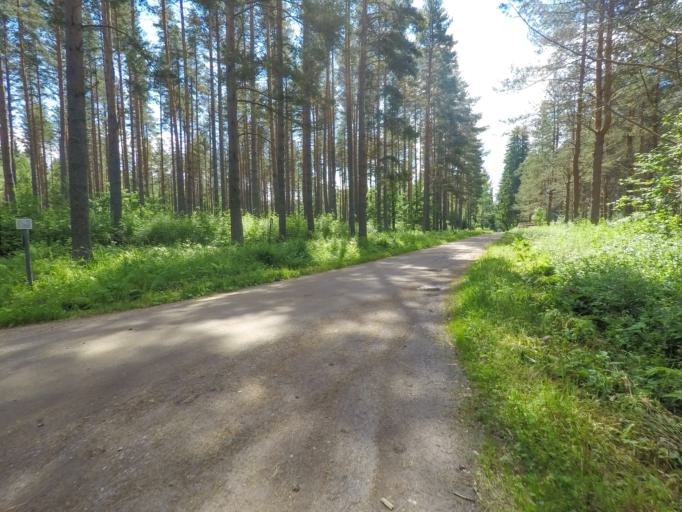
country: FI
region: Southern Savonia
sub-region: Savonlinna
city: Punkaharju
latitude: 61.8057
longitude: 29.3215
